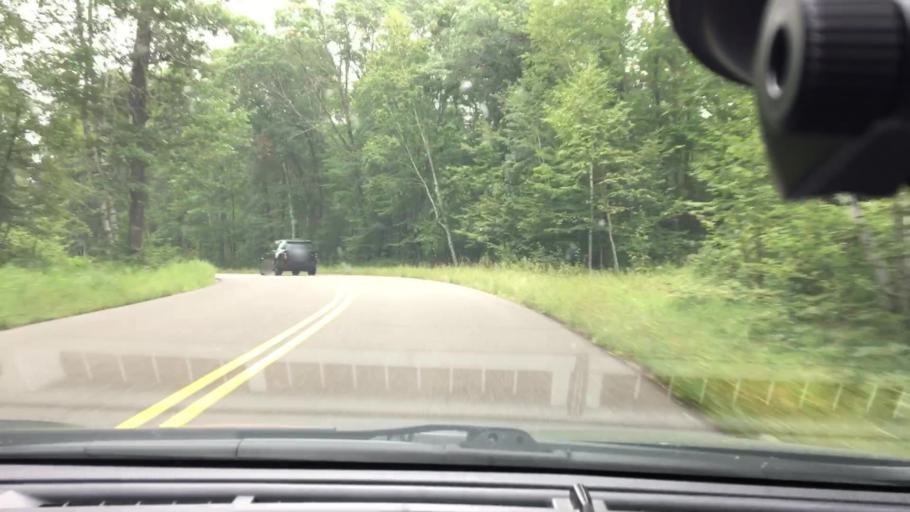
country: US
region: Minnesota
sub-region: Crow Wing County
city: Cross Lake
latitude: 46.6683
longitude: -94.0409
